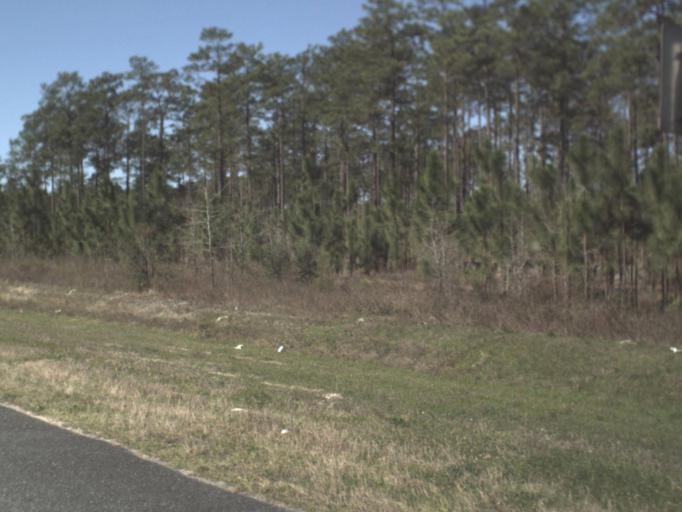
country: US
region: Florida
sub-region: Leon County
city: Woodville
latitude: 30.3437
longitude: -84.3155
